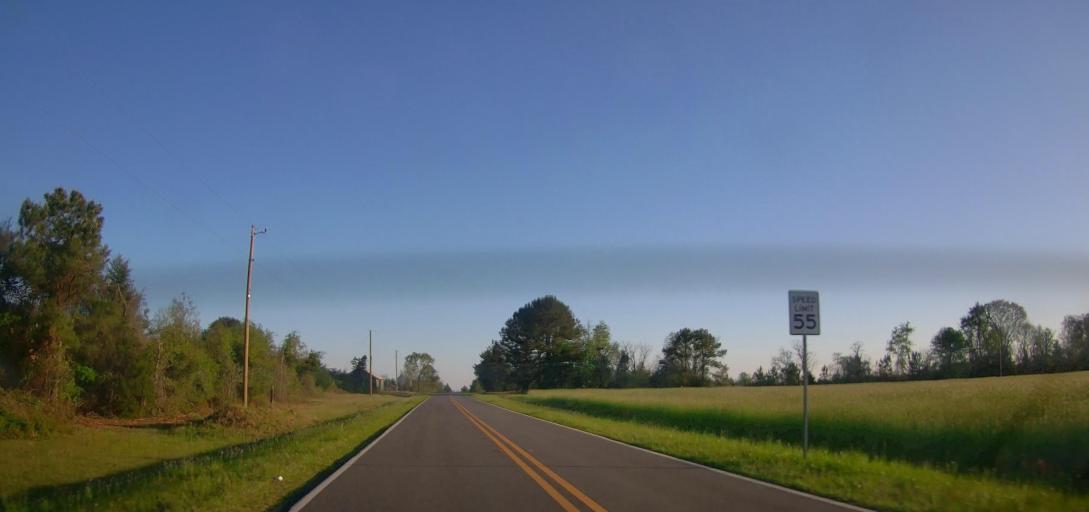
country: US
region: Georgia
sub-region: Marion County
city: Buena Vista
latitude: 32.4578
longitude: -84.4253
